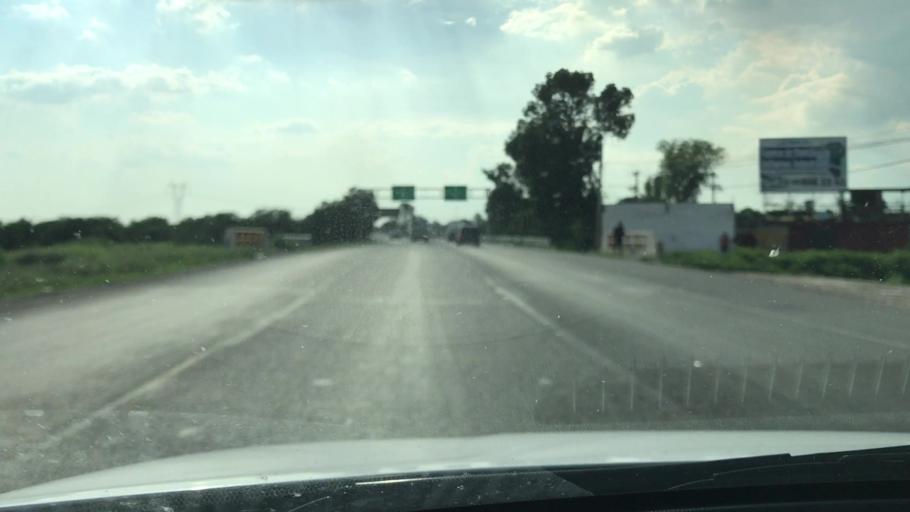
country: MX
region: Guanajuato
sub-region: Salamanca
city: El Divisador
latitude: 20.5578
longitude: -101.1637
